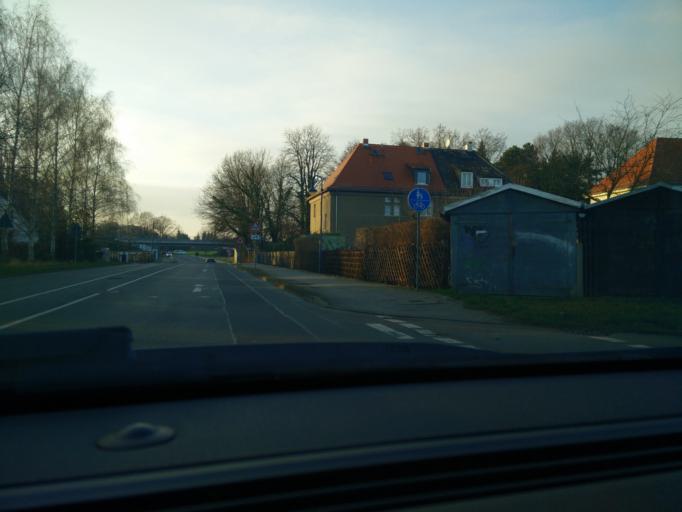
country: DE
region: Saxony
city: Taucha
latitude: 51.3324
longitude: 12.4612
